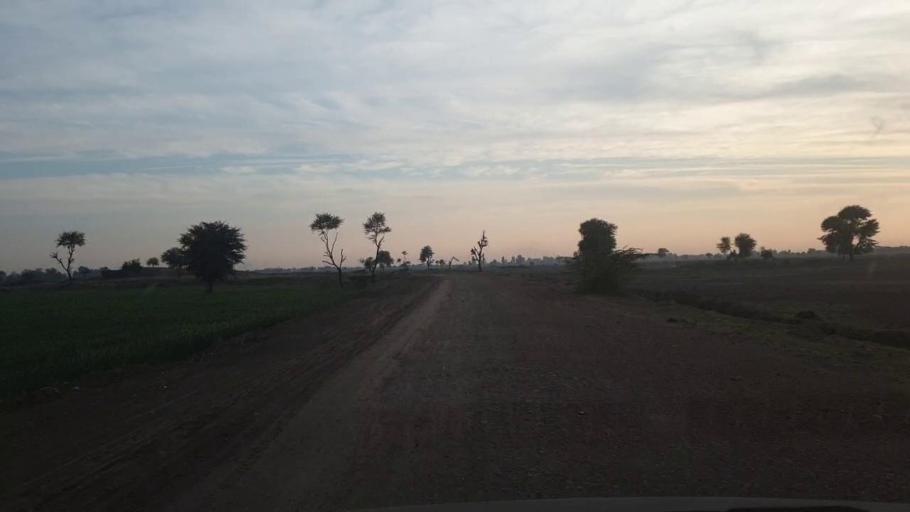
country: PK
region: Sindh
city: Shahpur Chakar
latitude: 26.0579
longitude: 68.5302
